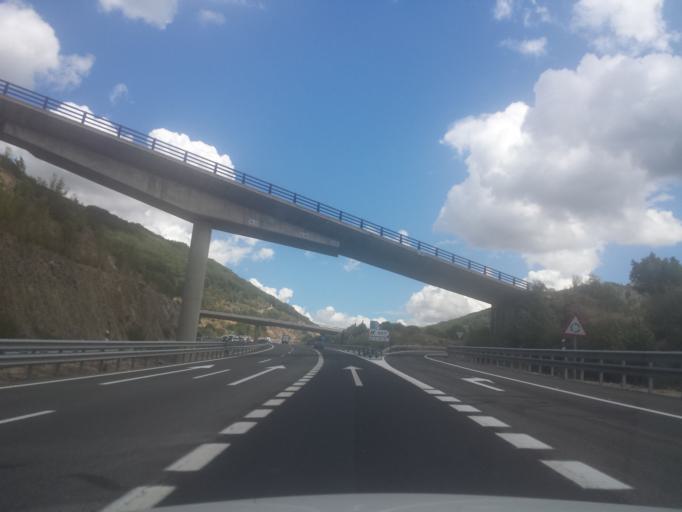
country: ES
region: Extremadura
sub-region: Provincia de Caceres
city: Banos de Montemayor
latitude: 40.3224
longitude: -5.8645
